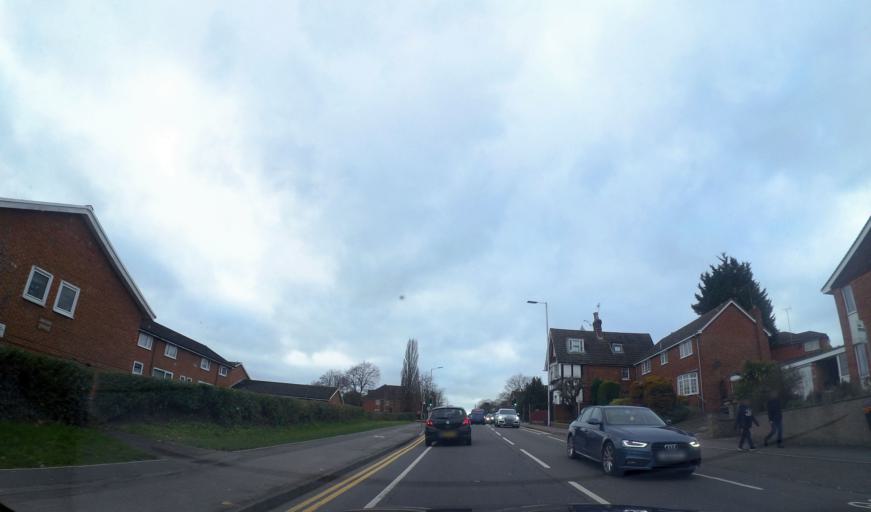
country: GB
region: England
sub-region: Reading
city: Reading
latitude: 51.4475
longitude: -0.9836
